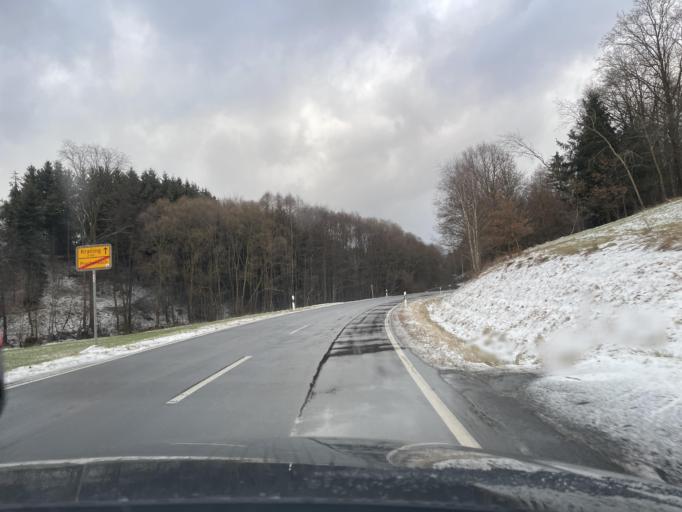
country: DE
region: Bavaria
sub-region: Lower Bavaria
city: Prackenbach
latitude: 49.0979
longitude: 12.8290
